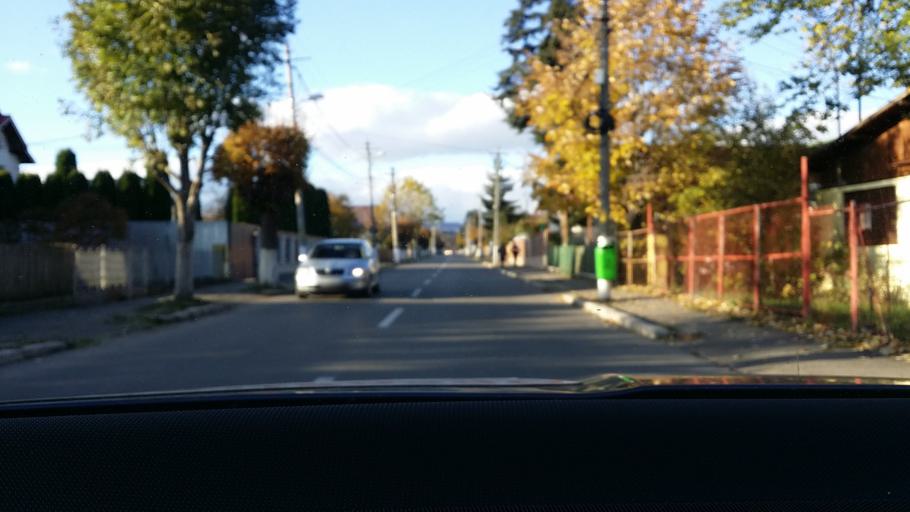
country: RO
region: Prahova
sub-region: Municipiul Campina
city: Campina
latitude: 45.1402
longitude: 25.7351
